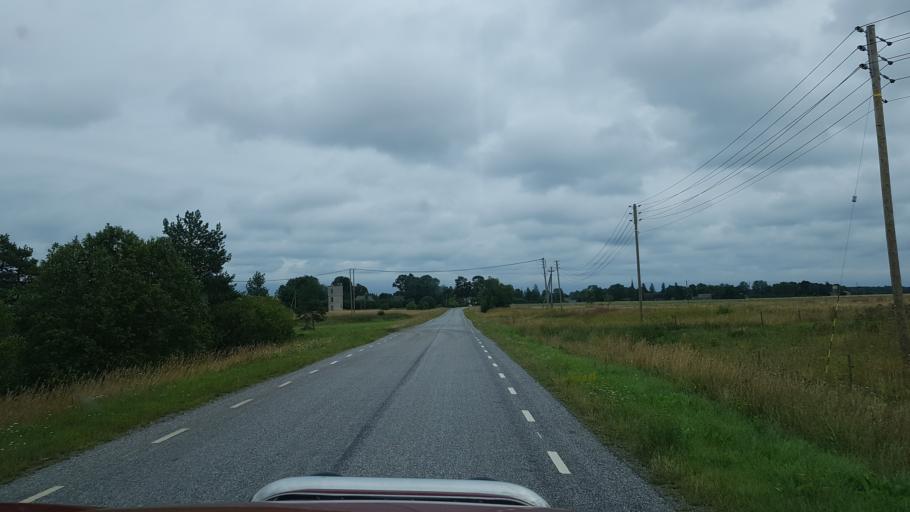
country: EE
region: Ida-Virumaa
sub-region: Puessi linn
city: Pussi
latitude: 59.3886
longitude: 27.0280
